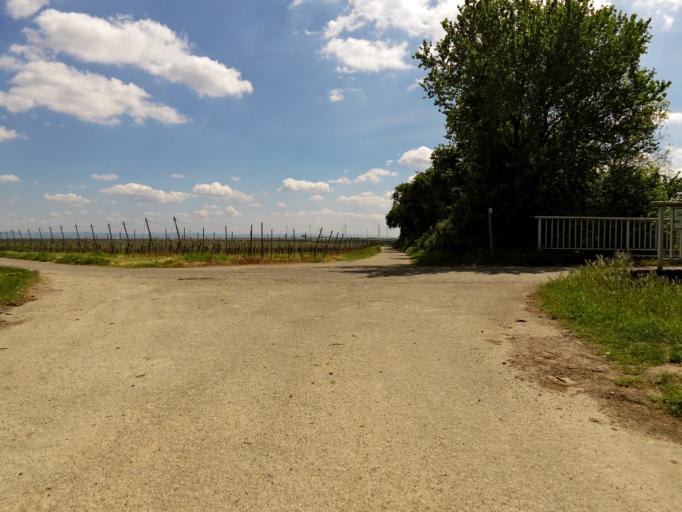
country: DE
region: Rheinland-Pfalz
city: Gundheim
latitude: 49.6840
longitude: 8.2479
